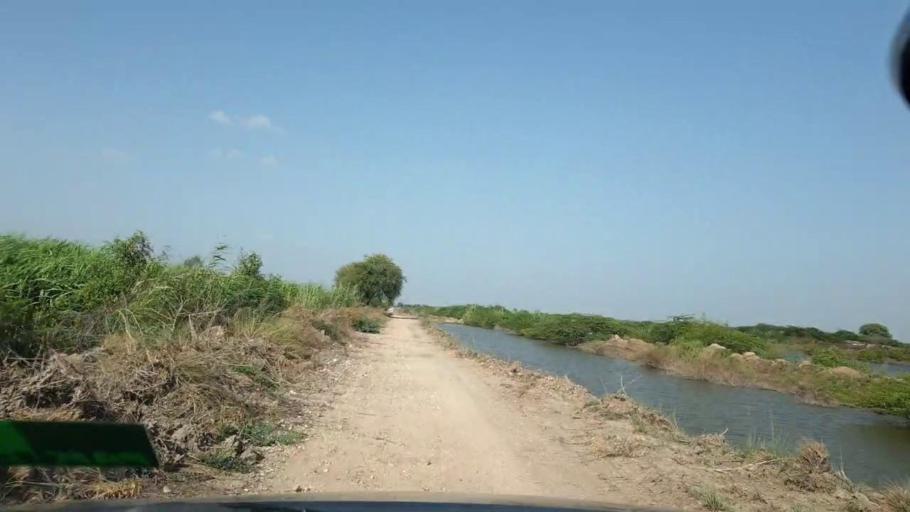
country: PK
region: Sindh
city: Tando Bago
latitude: 24.7019
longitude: 69.1998
